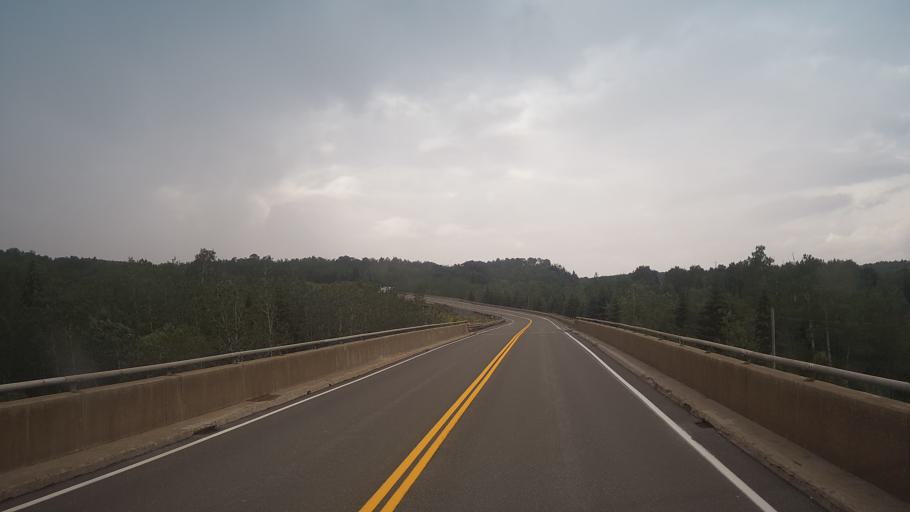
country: CA
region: Ontario
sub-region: Thunder Bay District
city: Thunder Bay
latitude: 48.5361
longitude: -89.5953
